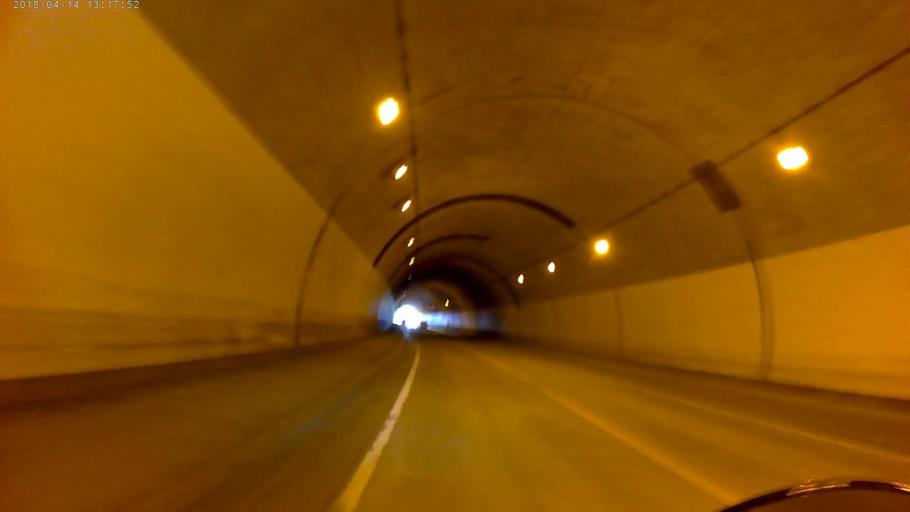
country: JP
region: Kanagawa
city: Hadano
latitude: 35.3402
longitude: 139.2266
